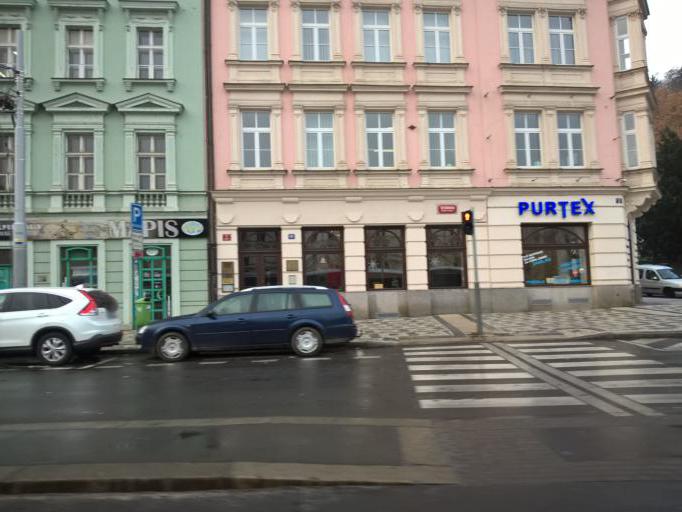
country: CZ
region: Praha
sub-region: Praha 1
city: Mala Strana
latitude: 50.0785
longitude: 14.4041
